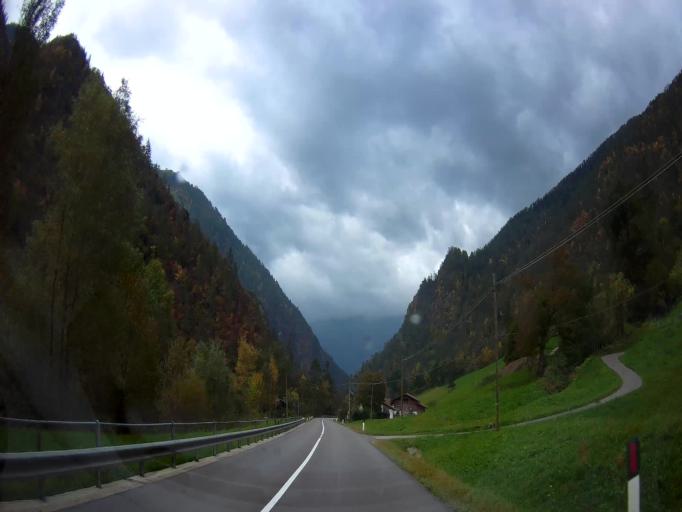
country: IT
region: Trentino-Alto Adige
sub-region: Bolzano
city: Certosa
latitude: 46.6759
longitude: 10.9388
